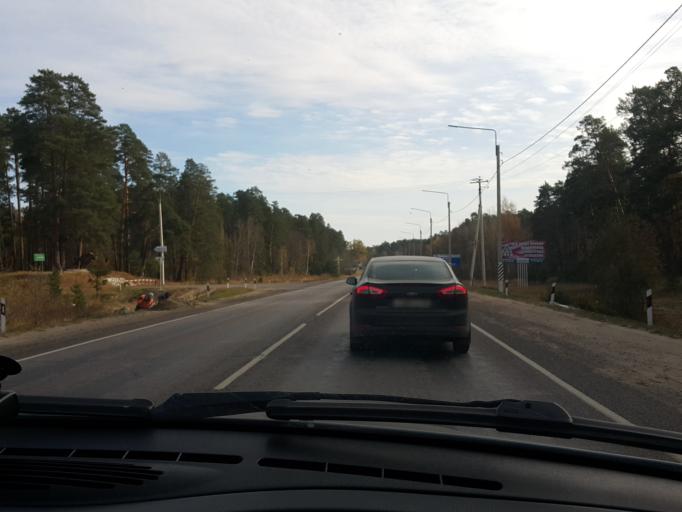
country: RU
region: Tambov
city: Donskoye
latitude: 52.7094
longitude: 41.5315
